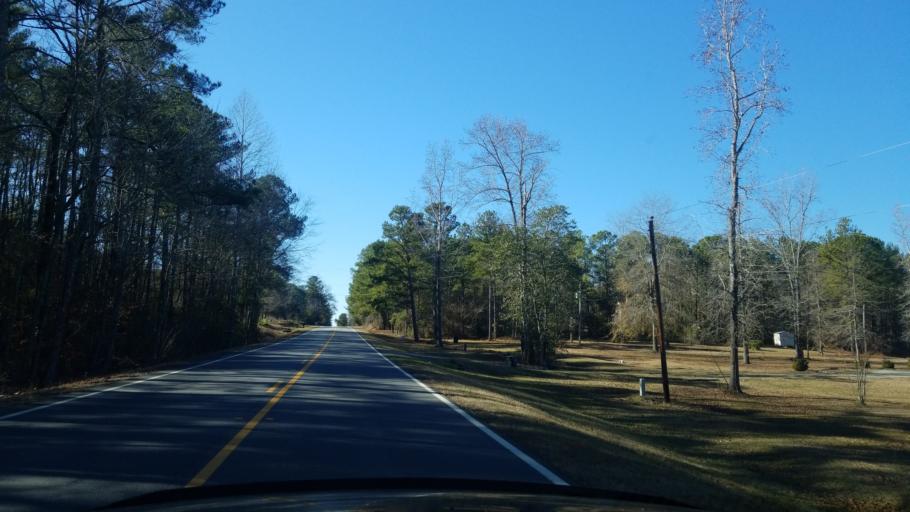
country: US
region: Georgia
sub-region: Harris County
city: Hamilton
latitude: 32.6321
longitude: -84.7418
